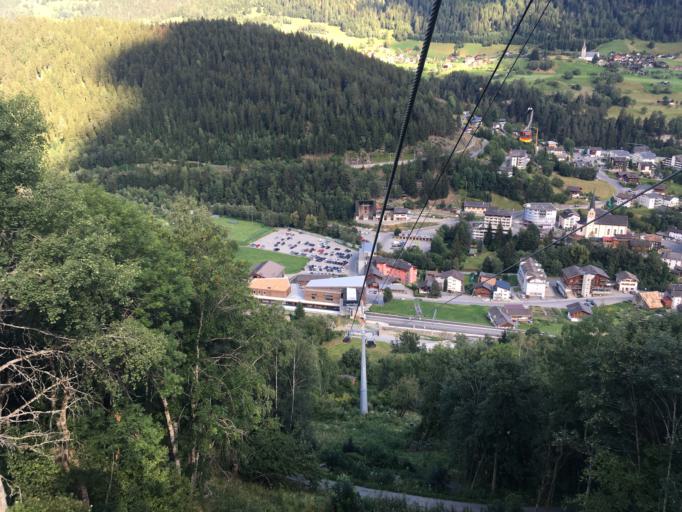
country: CH
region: Valais
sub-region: Goms District
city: Fiesch
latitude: 46.4070
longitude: 8.1300
